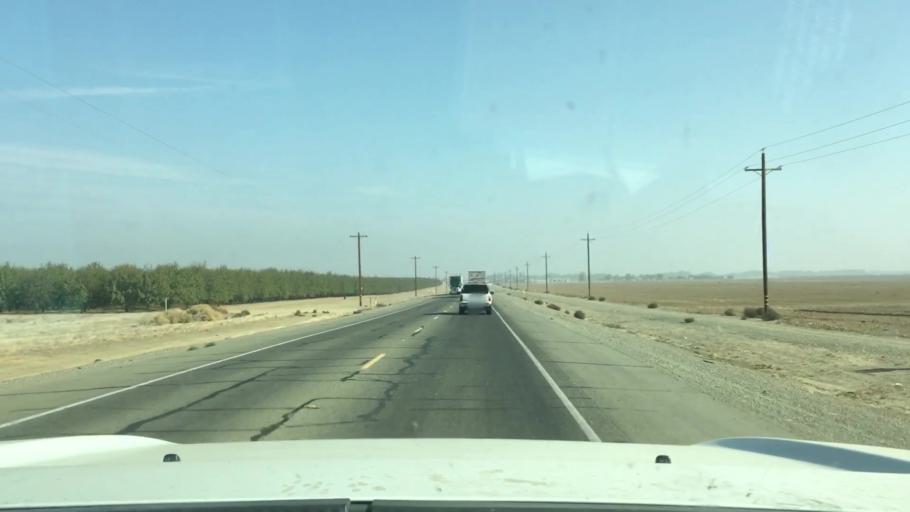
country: US
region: California
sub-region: Kern County
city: Lost Hills
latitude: 35.6160
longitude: -119.6820
